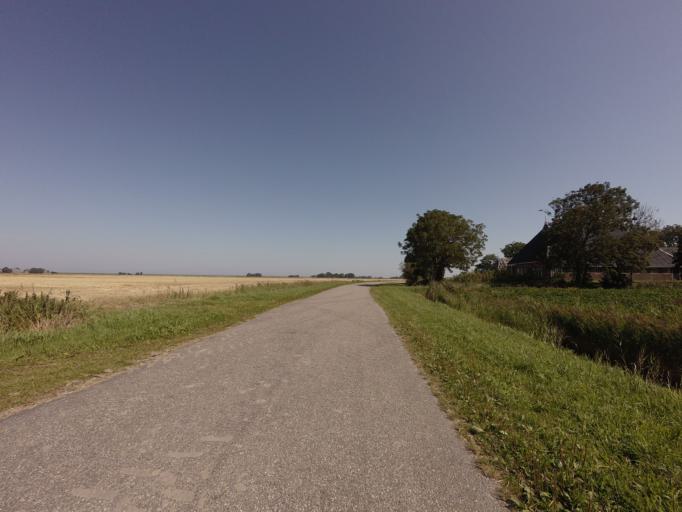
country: NL
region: Friesland
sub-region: Gemeente Dongeradeel
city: Holwerd
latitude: 53.3665
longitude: 5.9314
